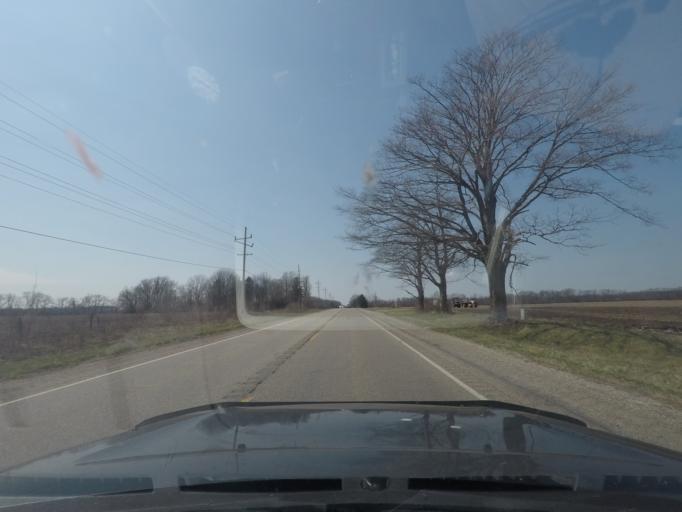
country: US
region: Indiana
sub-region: LaPorte County
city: LaPorte
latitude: 41.5914
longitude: -86.7606
